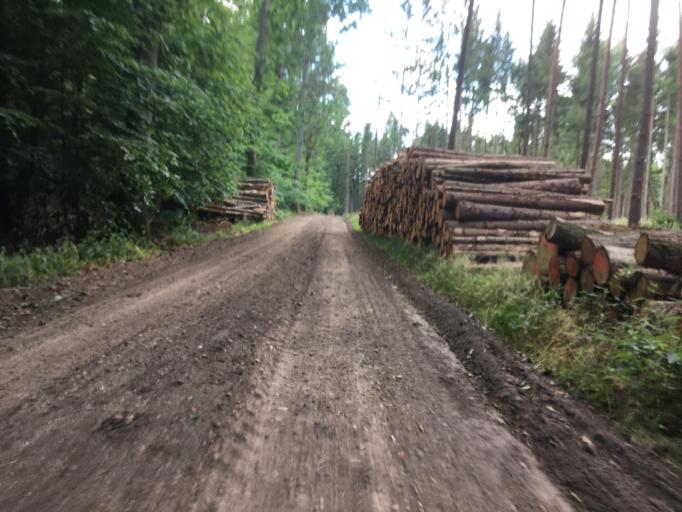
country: DE
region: Brandenburg
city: Joachimsthal
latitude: 52.9210
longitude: 13.7470
